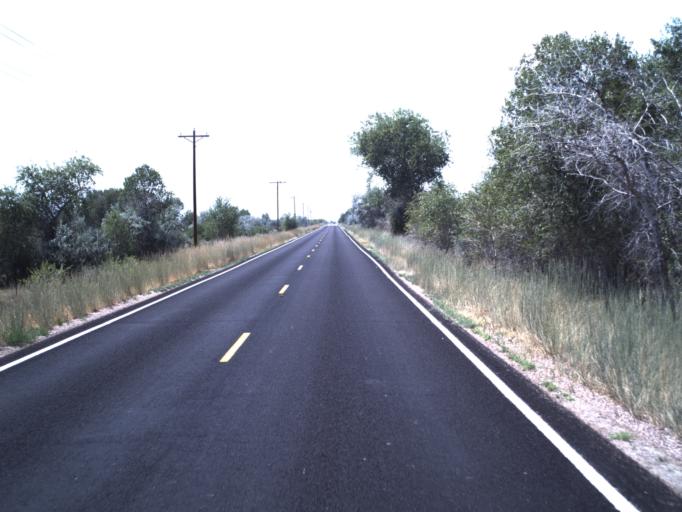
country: US
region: Utah
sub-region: Duchesne County
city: Roosevelt
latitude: 40.4038
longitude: -109.8853
